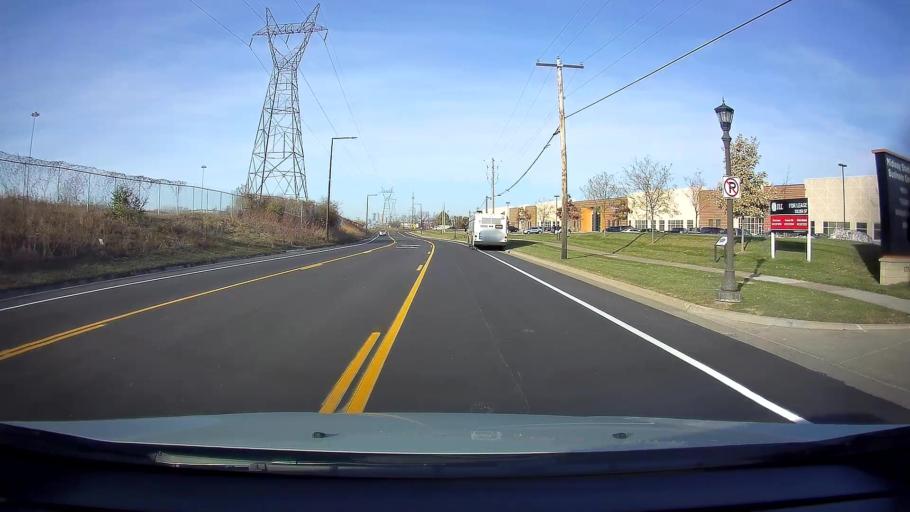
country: US
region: Minnesota
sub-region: Ramsey County
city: Falcon Heights
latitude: 44.9718
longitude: -93.1744
